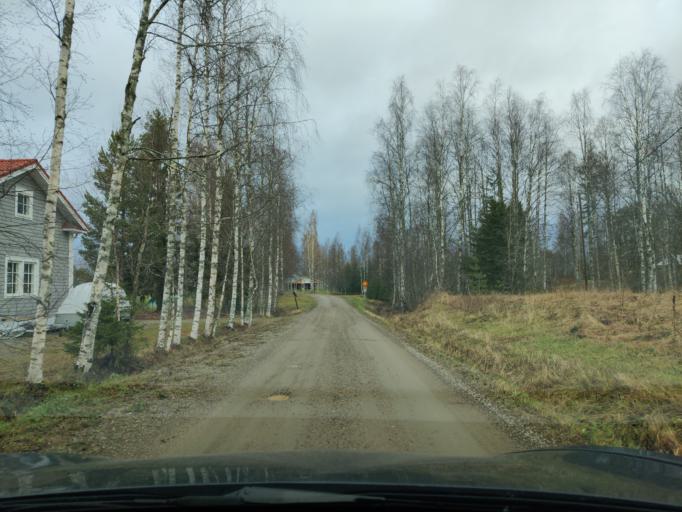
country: FI
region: Northern Savo
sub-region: Ylae-Savo
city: Kiuruvesi
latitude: 63.6398
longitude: 26.6549
